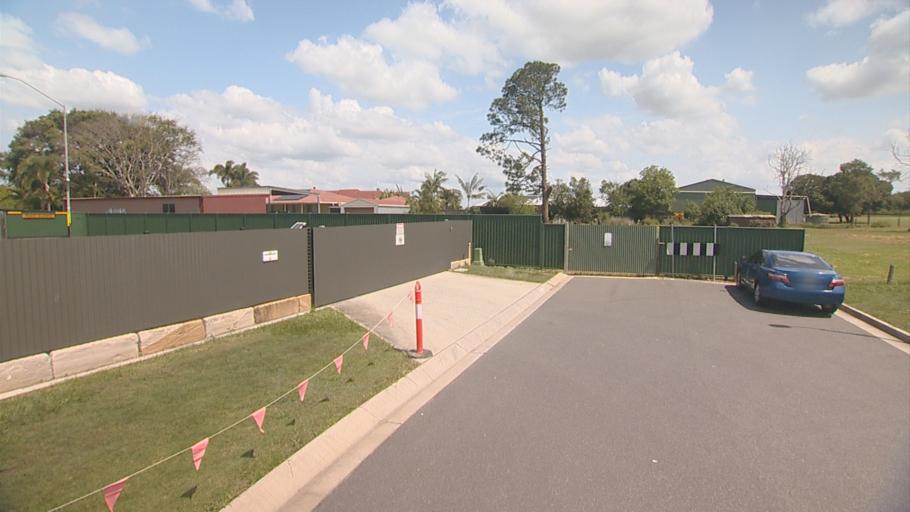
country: AU
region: Queensland
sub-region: Logan
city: Rochedale South
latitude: -27.5992
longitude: 153.1084
